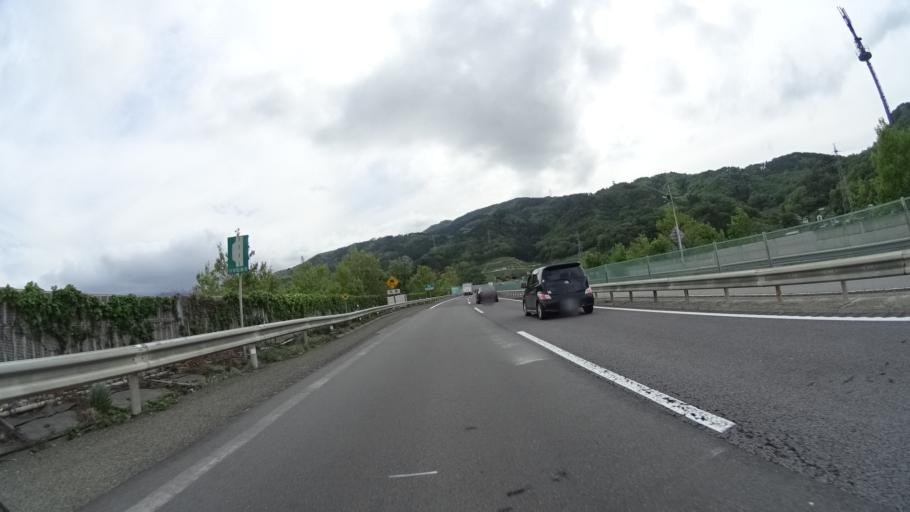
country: JP
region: Nagano
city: Nagano-shi
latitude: 36.5538
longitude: 138.1081
